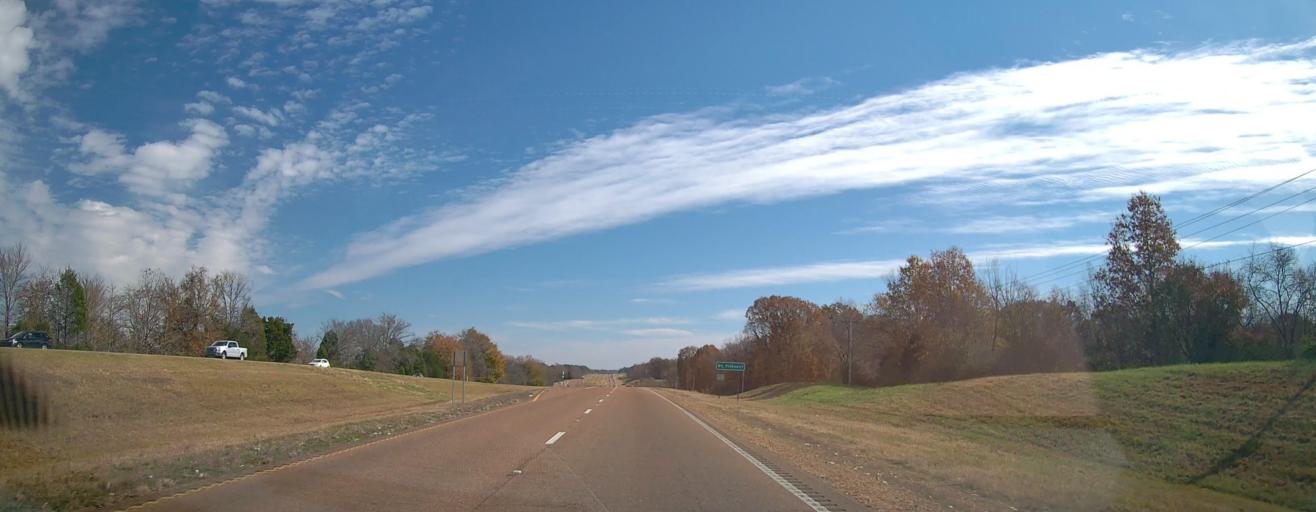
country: US
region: Tennessee
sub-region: Fayette County
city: Piperton
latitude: 34.9591
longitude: -89.5230
